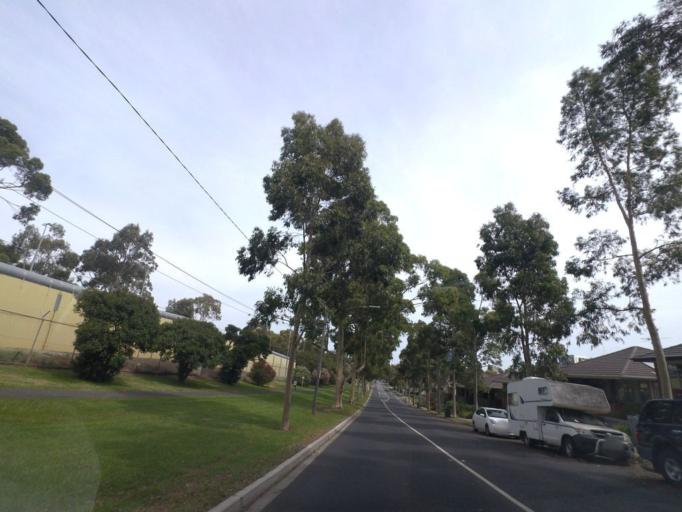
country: AU
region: Victoria
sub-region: Moonee Valley
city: Travancore
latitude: -37.7766
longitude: 144.9430
